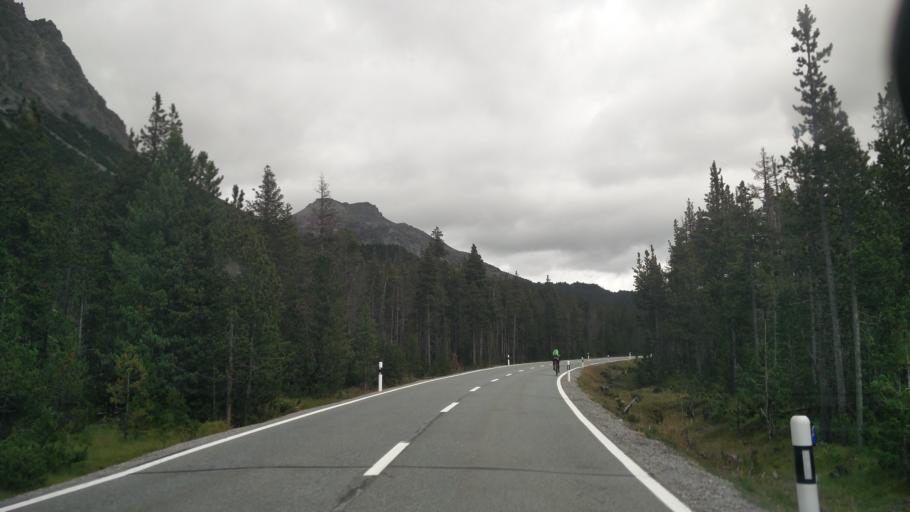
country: CH
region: Grisons
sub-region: Inn District
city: Scuol
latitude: 46.6537
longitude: 10.2541
